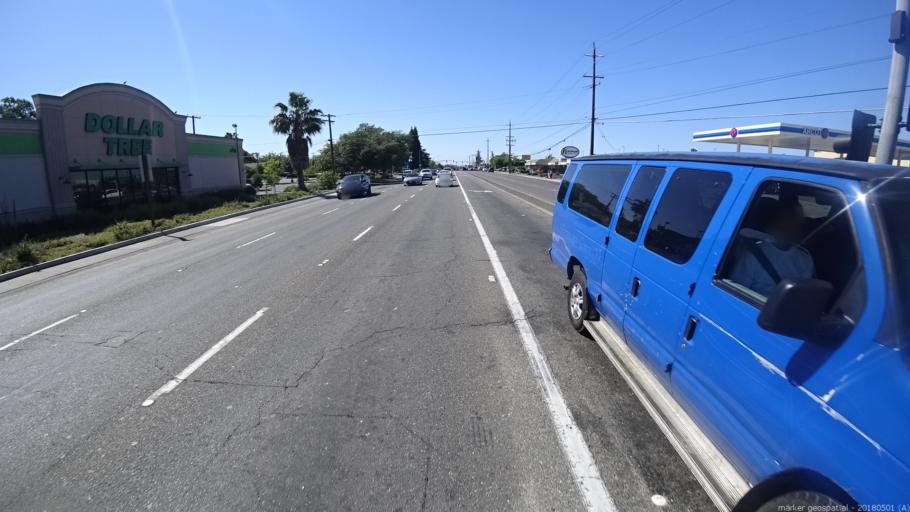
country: US
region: California
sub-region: Sacramento County
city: North Highlands
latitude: 38.6514
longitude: -121.3830
